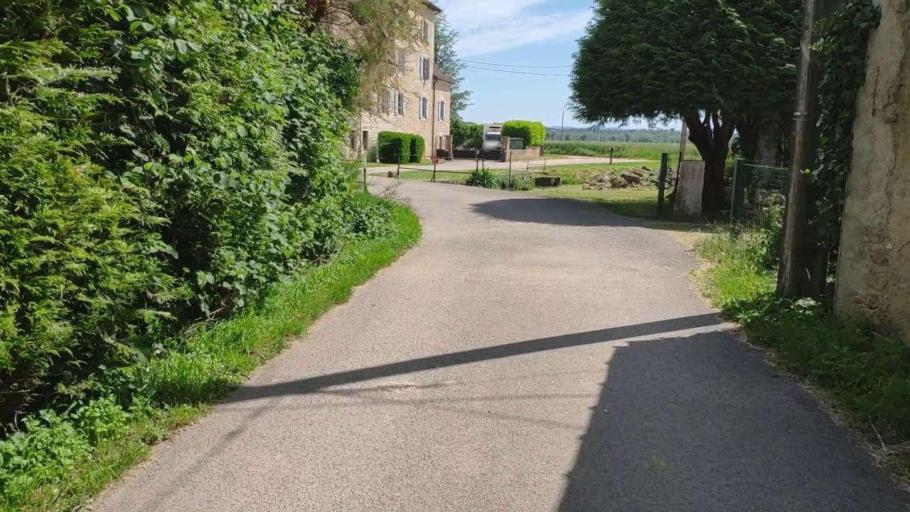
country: FR
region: Franche-Comte
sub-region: Departement du Jura
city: Bletterans
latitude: 46.7434
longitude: 5.4935
